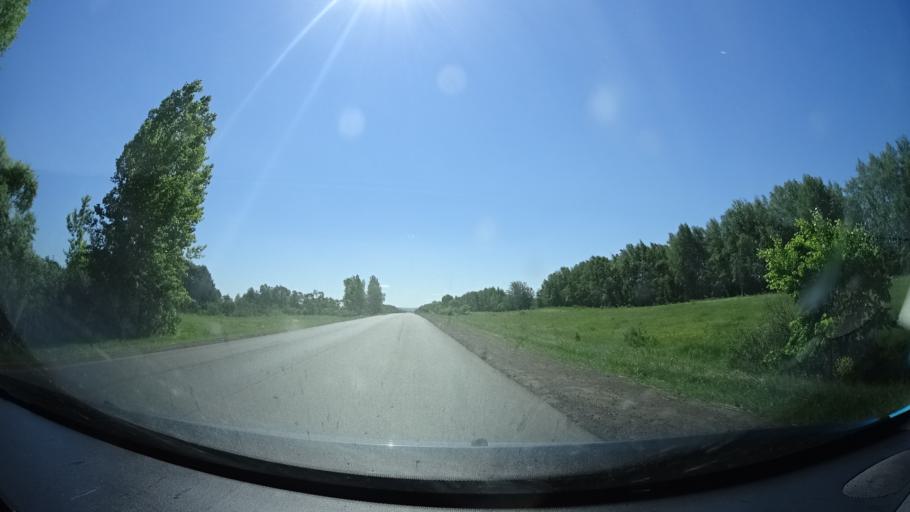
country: RU
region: Bashkortostan
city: Birsk
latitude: 55.2615
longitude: 55.7397
